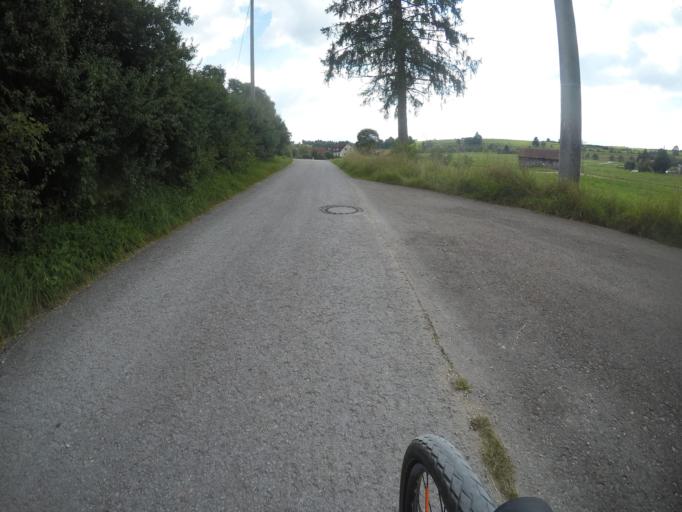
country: DE
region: Baden-Wuerttemberg
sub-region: Tuebingen Region
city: Munsingen
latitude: 48.4339
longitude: 9.4887
